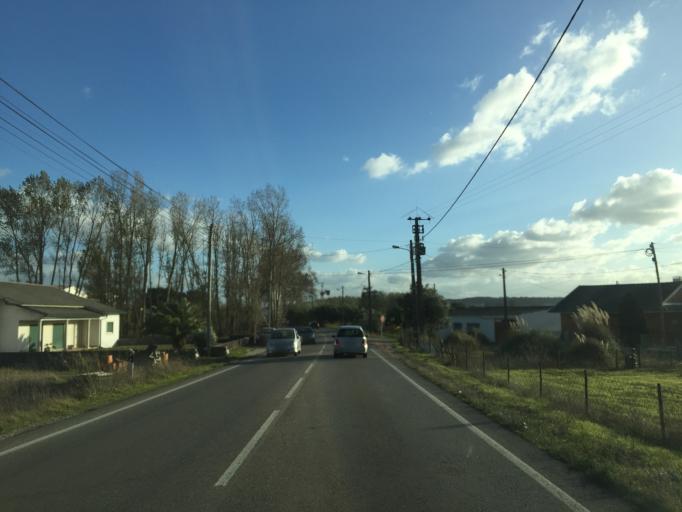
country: PT
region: Leiria
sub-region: Leiria
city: Amor
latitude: 39.8054
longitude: -8.8396
